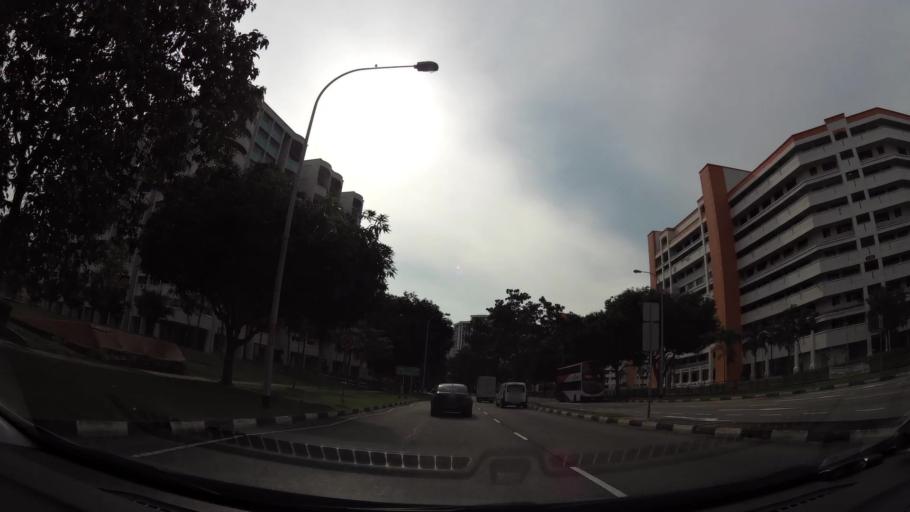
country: SG
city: Singapore
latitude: 1.3767
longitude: 103.8924
